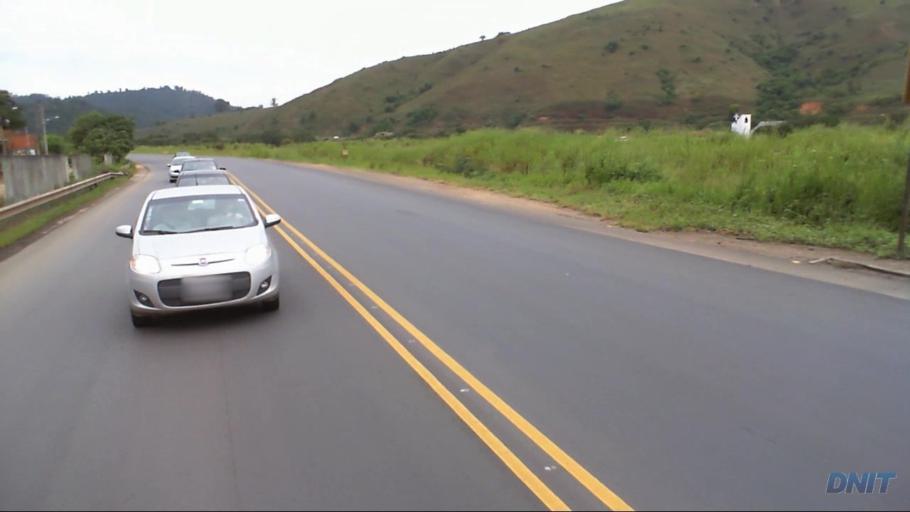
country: BR
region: Minas Gerais
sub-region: Coronel Fabriciano
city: Coronel Fabriciano
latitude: -19.5338
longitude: -42.5981
